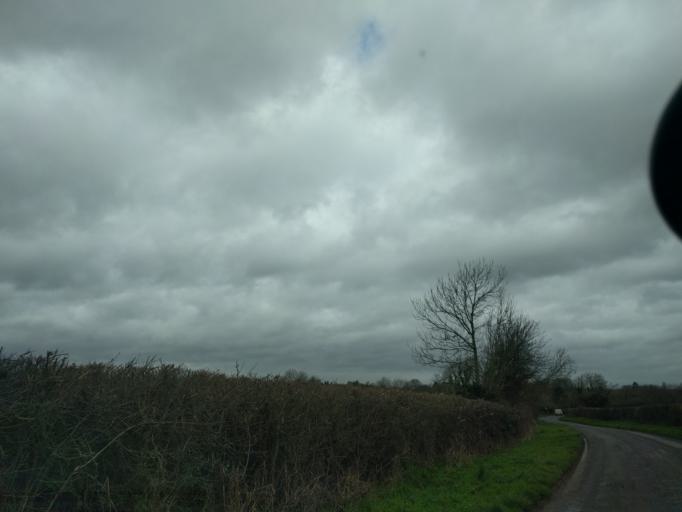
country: GB
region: England
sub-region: Wiltshire
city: Norton
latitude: 51.5690
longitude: -2.2007
